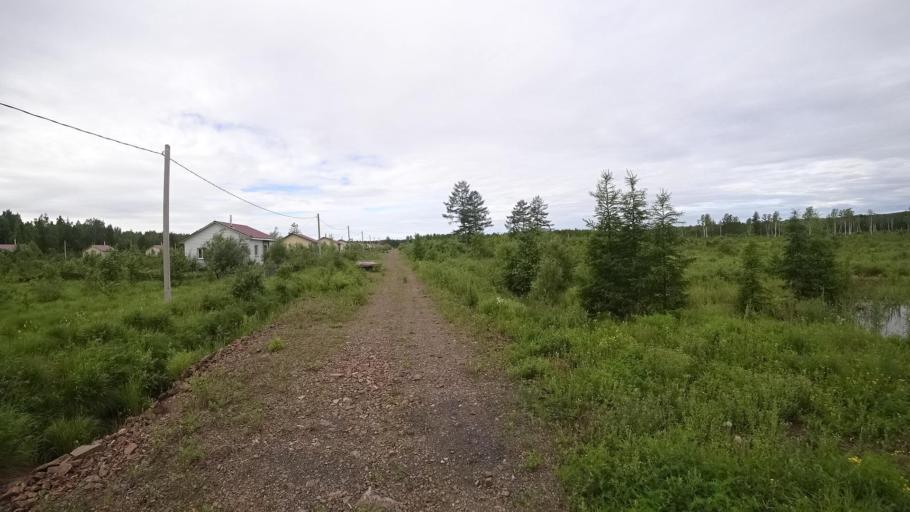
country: RU
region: Khabarovsk Krai
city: Amursk
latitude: 49.8987
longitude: 136.1646
